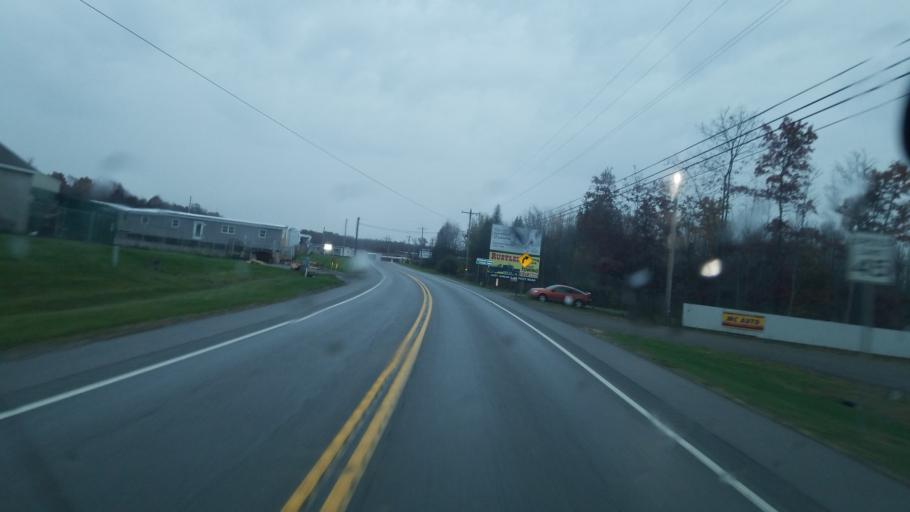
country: US
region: Pennsylvania
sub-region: Clarion County
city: Marianne
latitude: 41.2316
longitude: -79.4308
